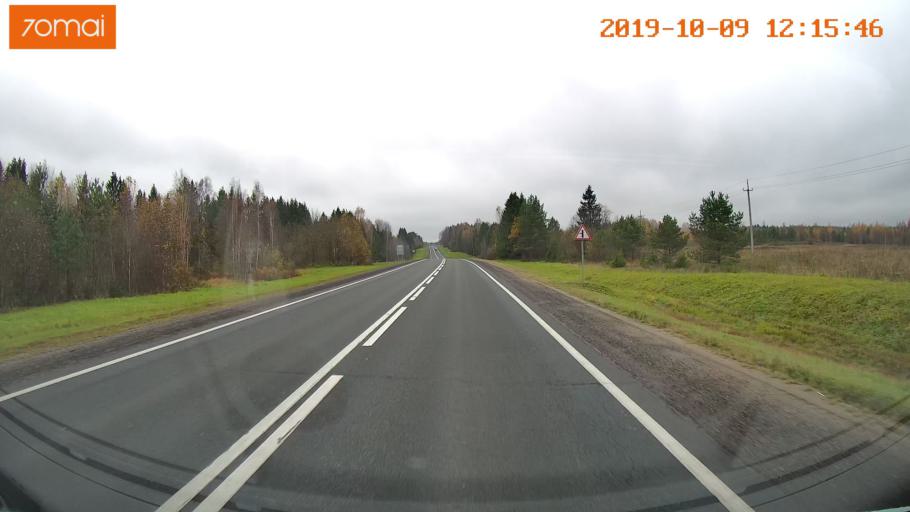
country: RU
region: Jaroslavl
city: Prechistoye
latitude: 58.4785
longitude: 40.3225
